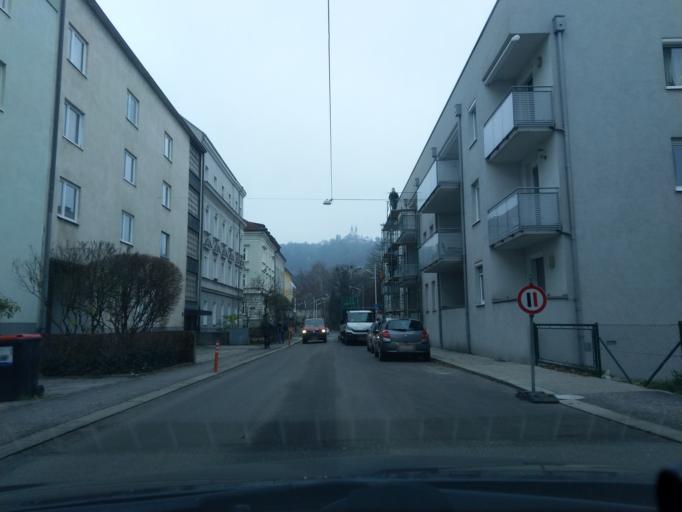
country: AT
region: Upper Austria
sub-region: Linz Stadt
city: Linz
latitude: 48.3150
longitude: 14.2751
